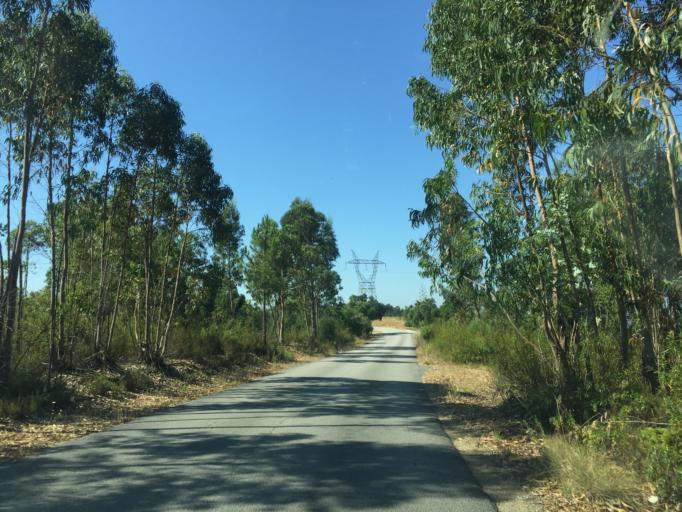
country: PT
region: Santarem
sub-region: Tomar
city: Tomar
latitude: 39.5672
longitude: -8.3204
